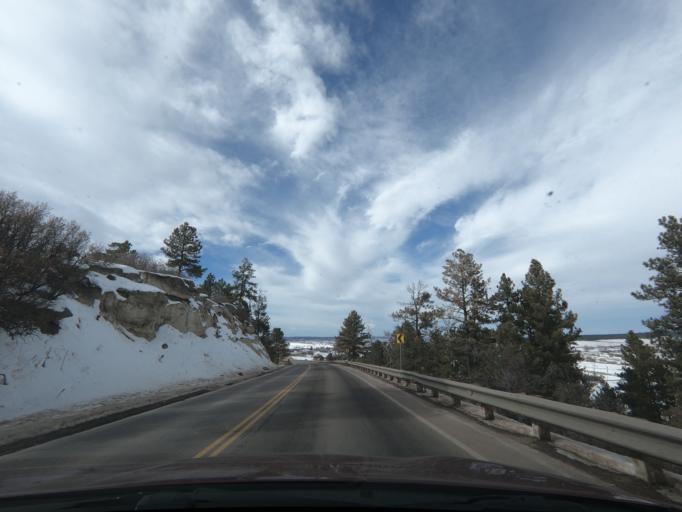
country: US
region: Colorado
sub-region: Elbert County
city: Ponderosa Park
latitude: 39.3504
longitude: -104.7366
